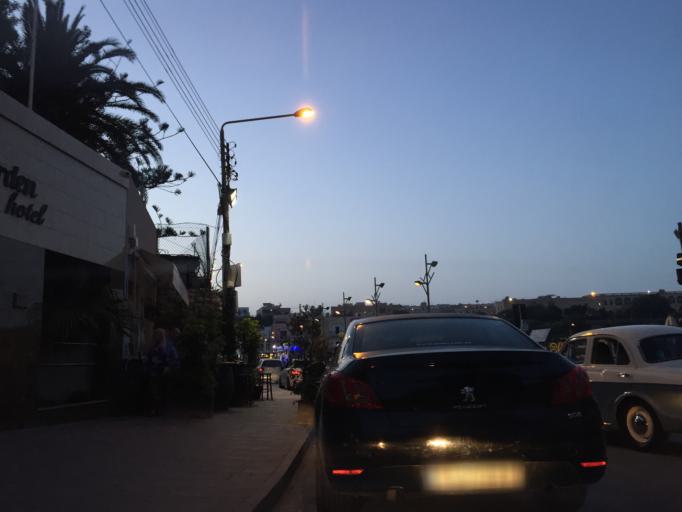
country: MT
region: Saint Julian
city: San Giljan
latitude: 35.9251
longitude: 14.4882
